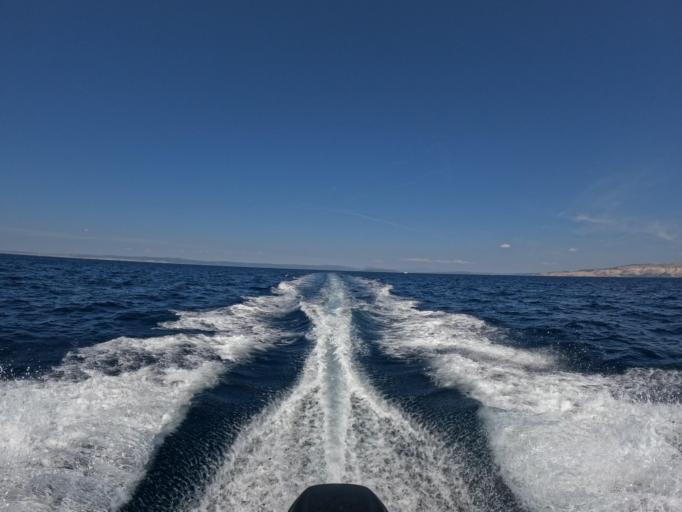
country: HR
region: Primorsko-Goranska
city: Lopar
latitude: 44.8663
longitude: 14.6783
